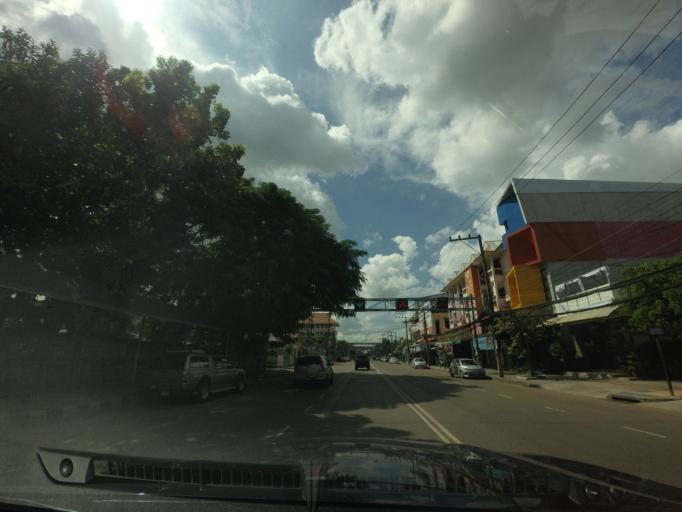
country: TH
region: Changwat Udon Thani
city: Udon Thani
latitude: 17.4083
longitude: 102.7807
